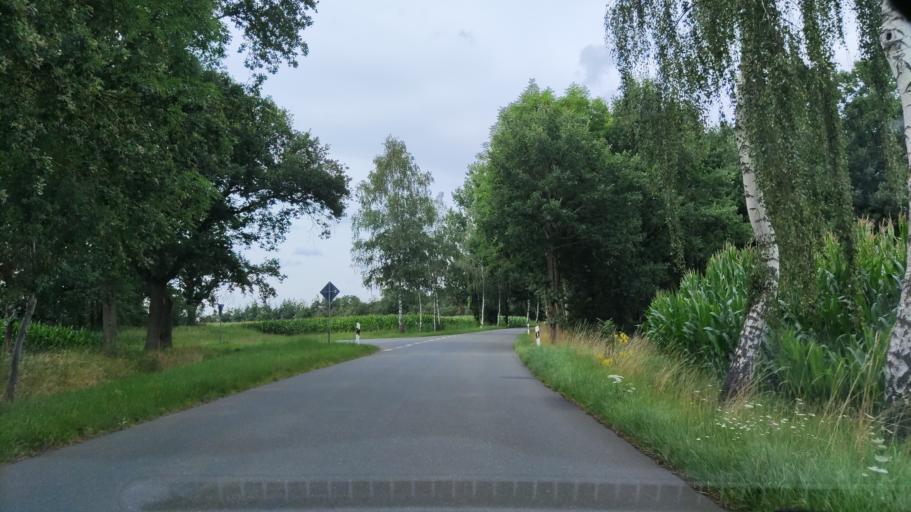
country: DE
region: Lower Saxony
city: Dannenberg
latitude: 53.0879
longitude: 11.1286
